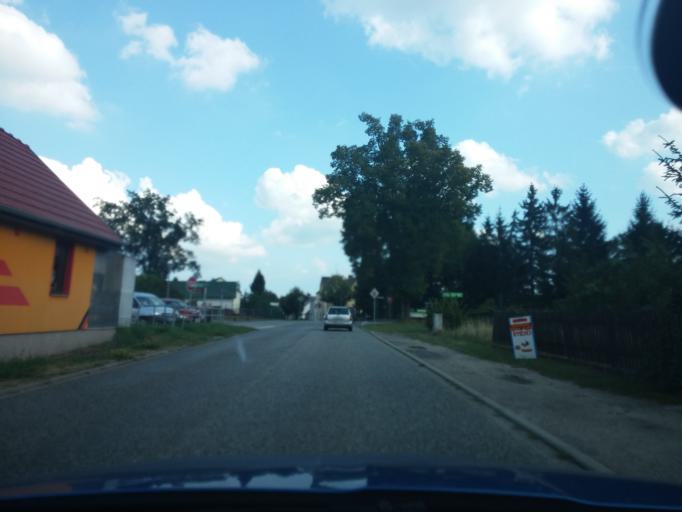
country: DE
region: Brandenburg
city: Halbe
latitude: 52.1073
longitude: 13.6945
